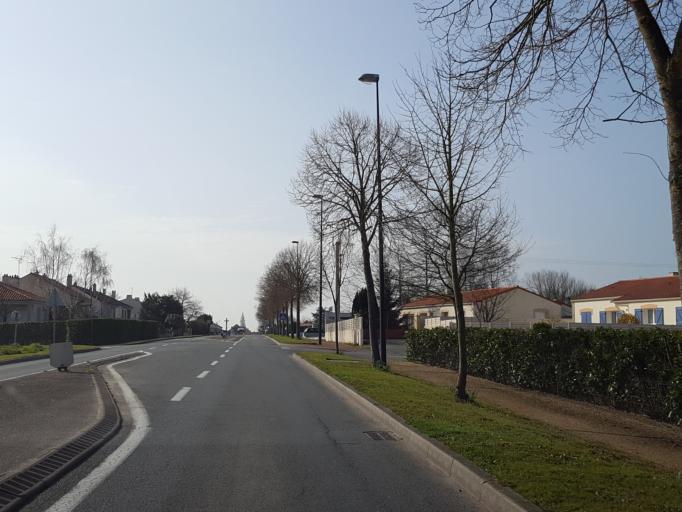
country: FR
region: Pays de la Loire
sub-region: Departement de la Vendee
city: Les Lucs-sur-Boulogne
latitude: 46.8489
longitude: -1.4948
